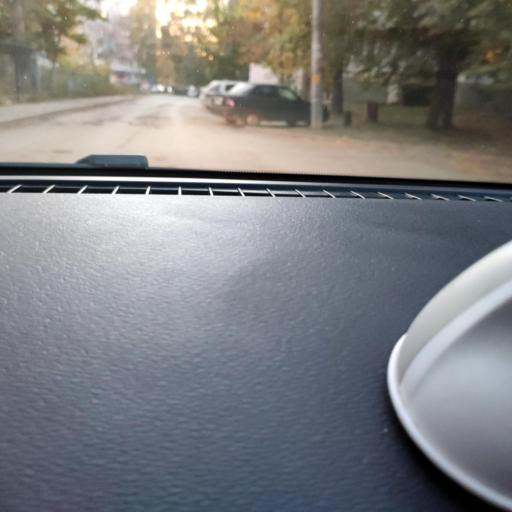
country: RU
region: Samara
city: Samara
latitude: 53.2373
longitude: 50.2067
